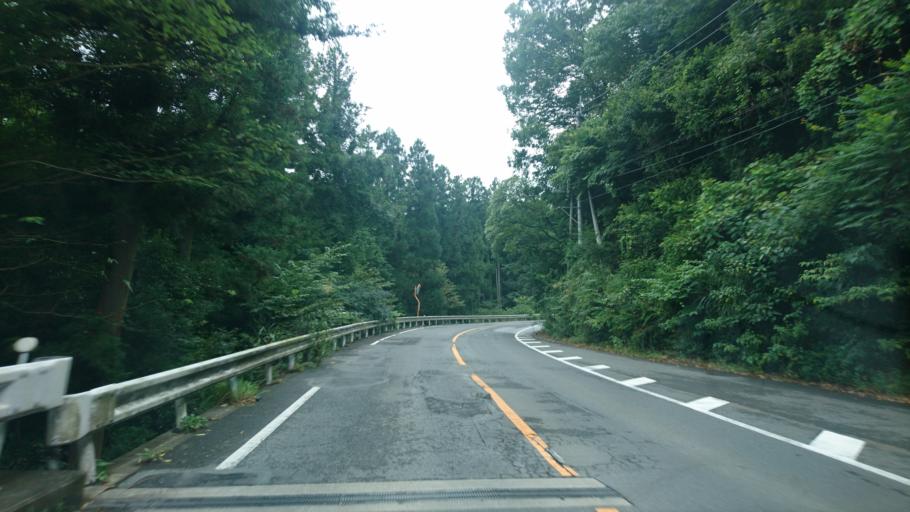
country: JP
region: Gunma
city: Omamacho-omama
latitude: 36.4921
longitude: 139.2731
